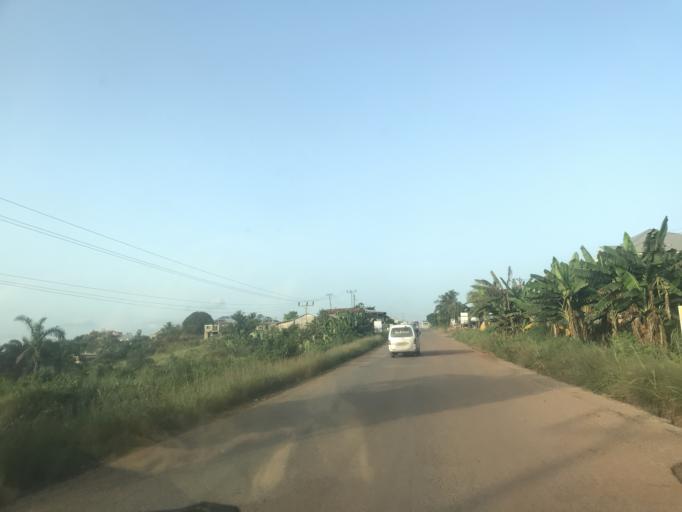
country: GH
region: Ashanti
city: Obuasi
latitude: 6.2029
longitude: -1.6082
